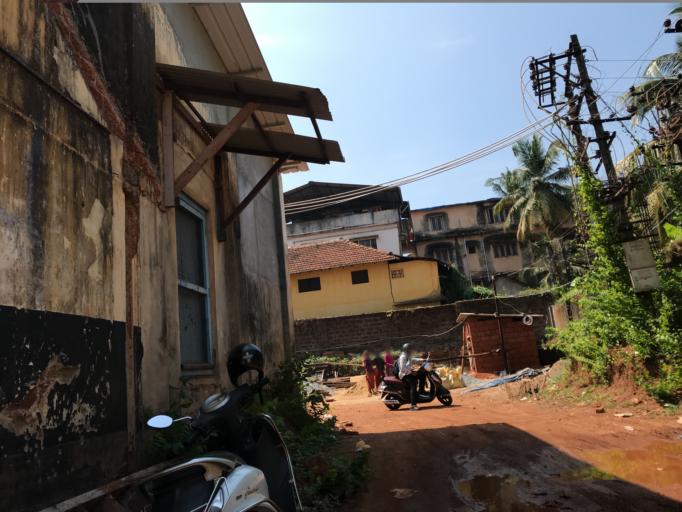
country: IN
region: Karnataka
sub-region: Dakshina Kannada
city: Mangalore
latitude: 12.8709
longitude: 74.8372
